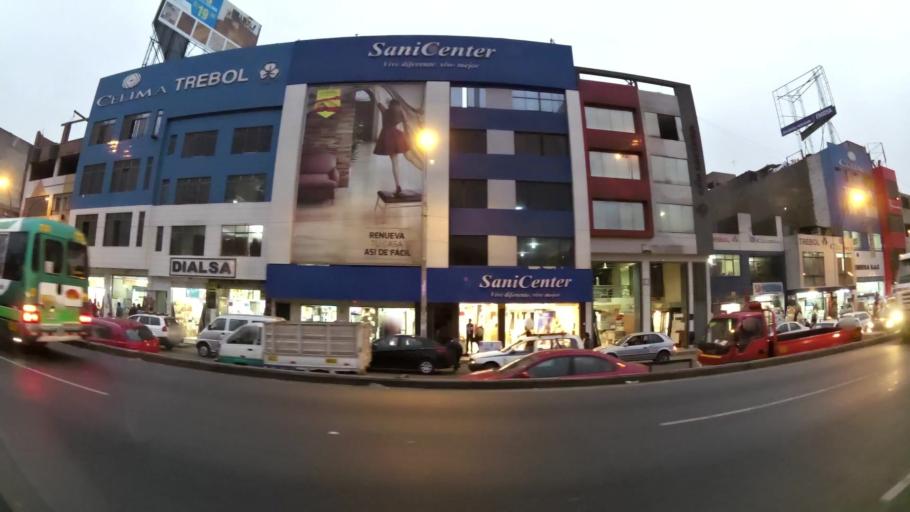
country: PE
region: Lima
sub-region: Lima
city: Independencia
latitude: -12.0194
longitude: -77.0594
